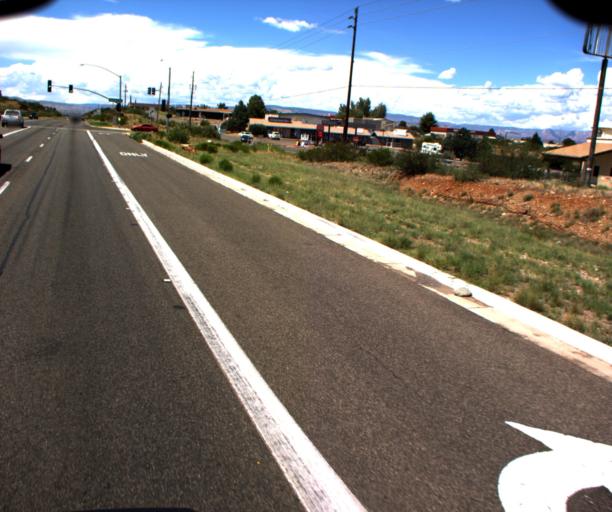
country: US
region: Arizona
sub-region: Yavapai County
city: Verde Village
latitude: 34.6915
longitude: -111.9821
